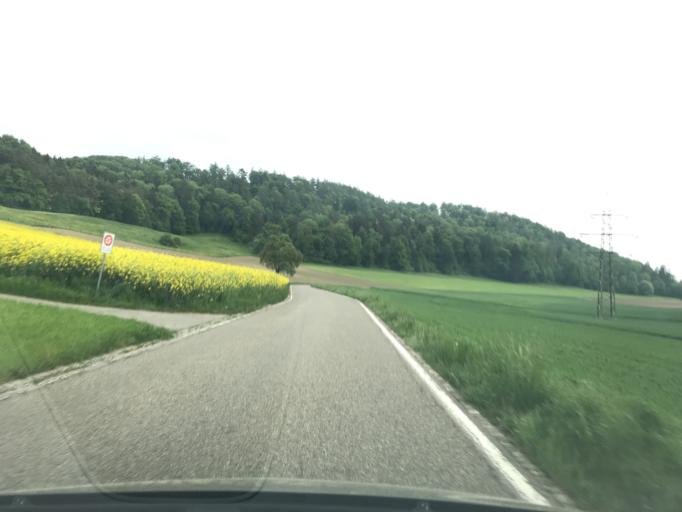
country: CH
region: Zurich
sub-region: Bezirk Winterthur
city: Wuelflingen (Kreis 6) / Niederfeld
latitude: 47.4956
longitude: 8.6831
